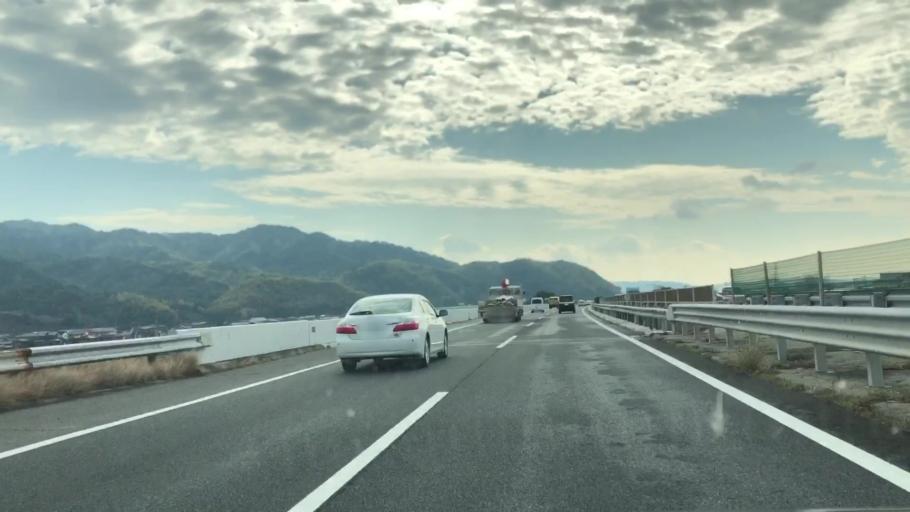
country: JP
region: Fukuoka
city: Setakamachi-takayanagi
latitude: 33.1794
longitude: 130.5176
